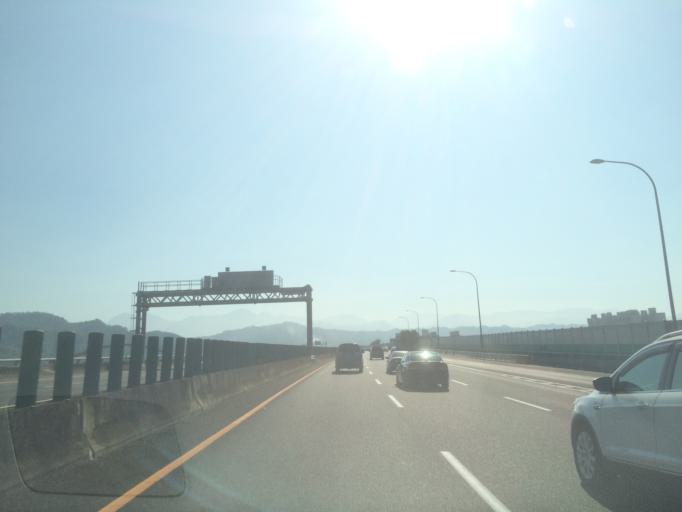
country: TW
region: Taiwan
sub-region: Nantou
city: Nantou
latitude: 23.9176
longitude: 120.6904
